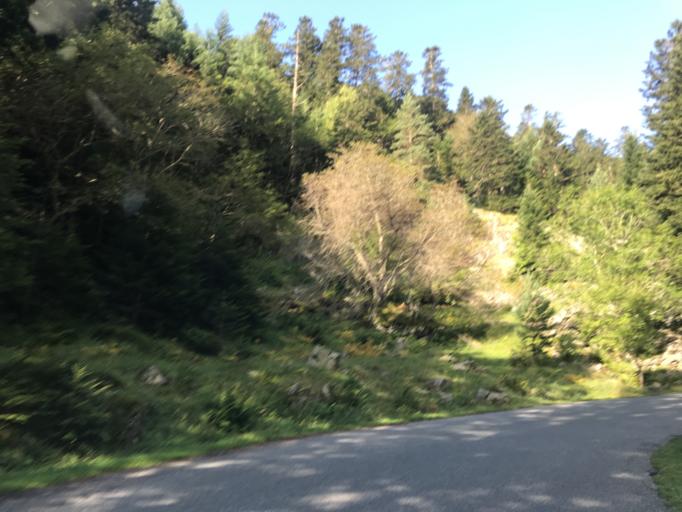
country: FR
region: Midi-Pyrenees
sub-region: Departement des Hautes-Pyrenees
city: Saint-Lary-Soulan
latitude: 42.8180
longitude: 0.1937
